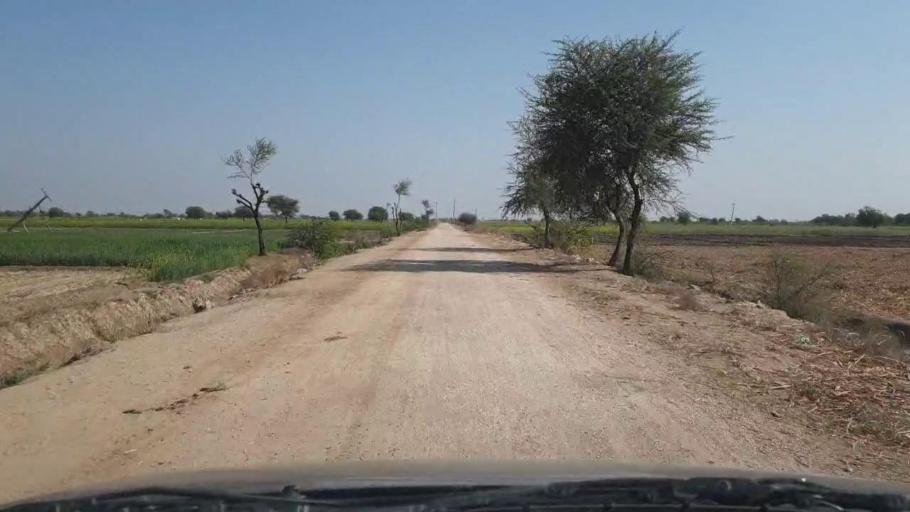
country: PK
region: Sindh
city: Samaro
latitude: 25.2004
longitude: 69.2884
